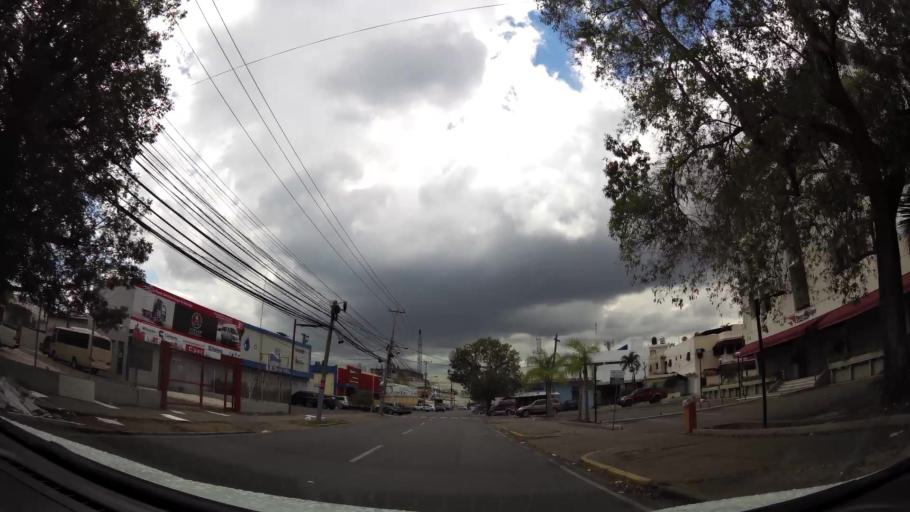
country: DO
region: Nacional
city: La Agustina
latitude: 18.4842
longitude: -69.9255
